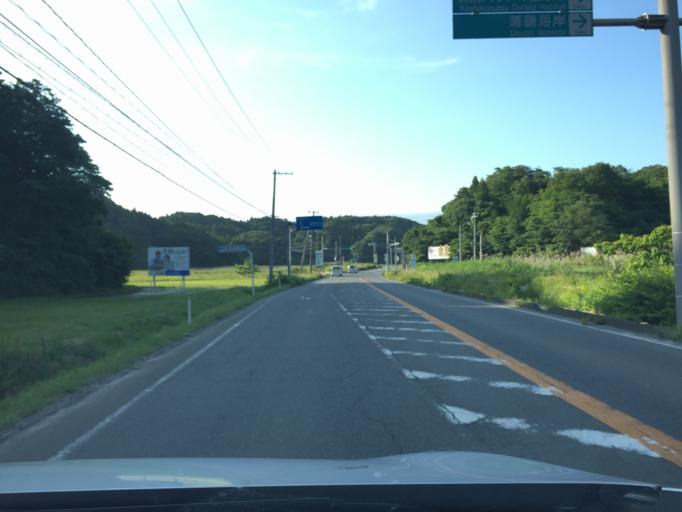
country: JP
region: Fukushima
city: Iwaki
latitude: 37.0037
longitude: 140.9670
